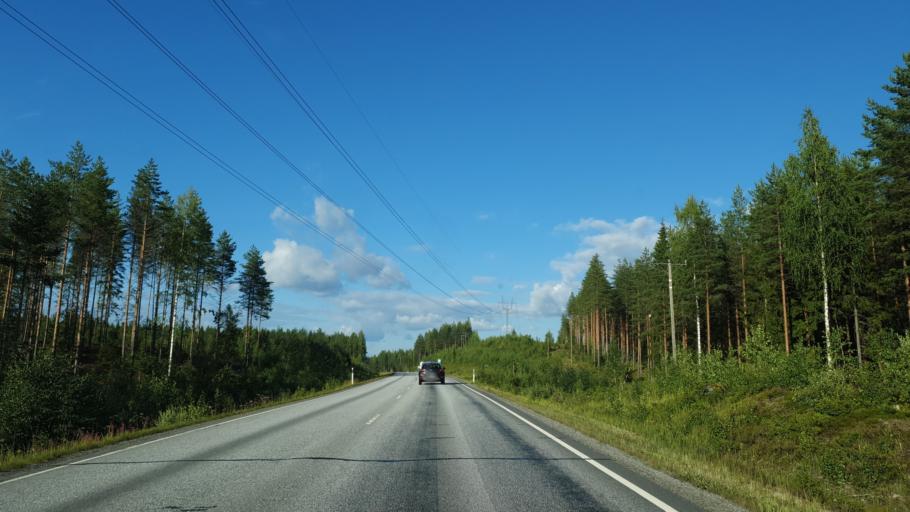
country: FI
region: North Karelia
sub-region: Joensuu
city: Outokumpu
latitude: 62.5371
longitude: 29.1142
